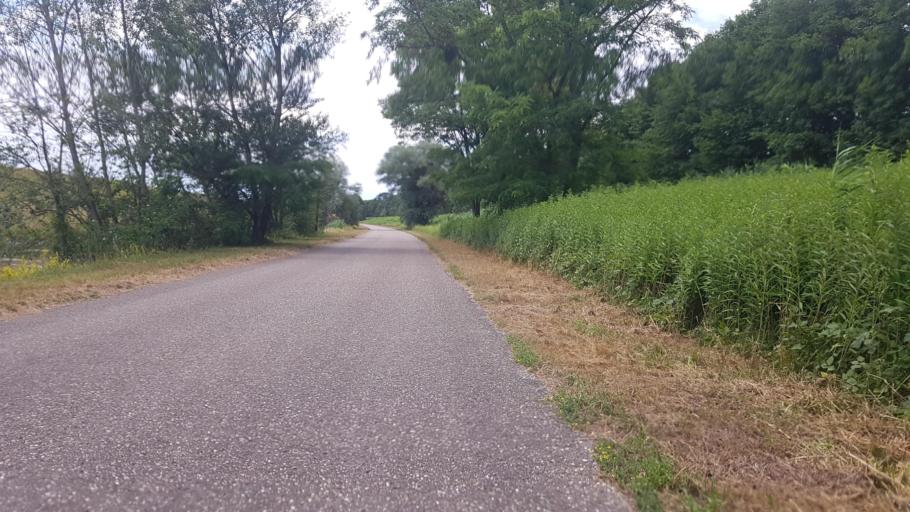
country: DE
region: Baden-Wuerttemberg
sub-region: Karlsruhe Region
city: Schwarzach
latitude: 48.7927
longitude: 8.0473
